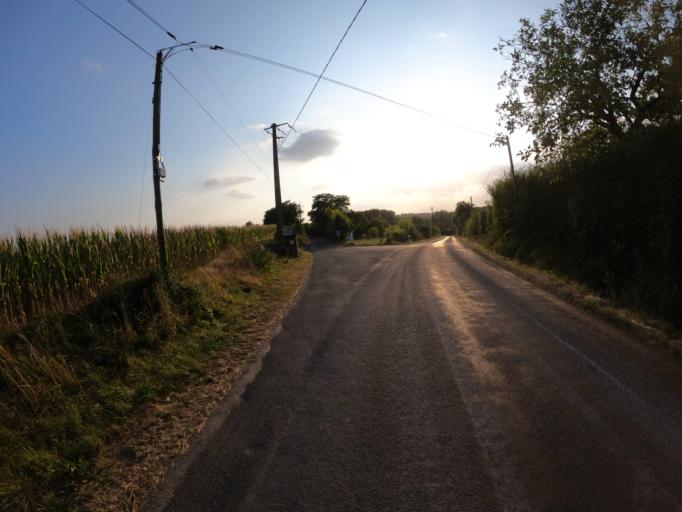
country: FR
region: Pays de la Loire
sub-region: Departement de la Sarthe
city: Brulon
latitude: 47.9456
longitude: -0.2325
